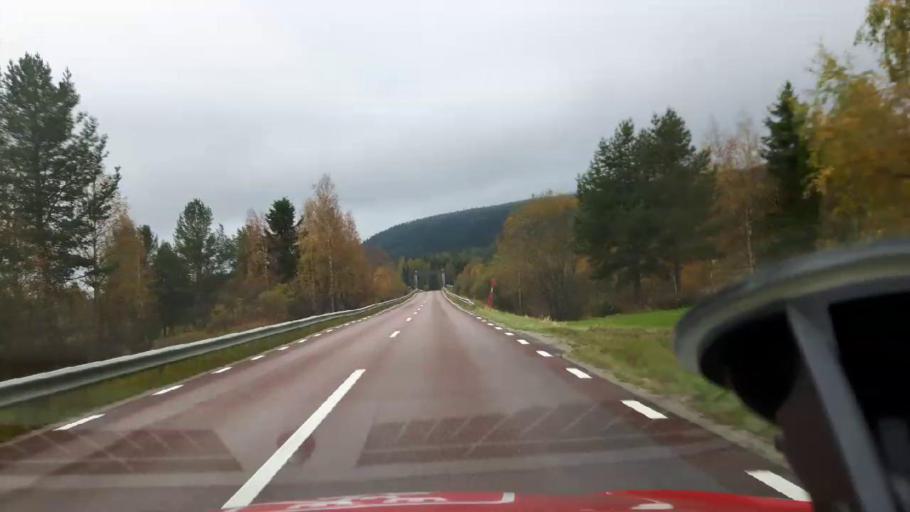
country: SE
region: Jaemtland
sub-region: Harjedalens Kommun
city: Sveg
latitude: 62.2763
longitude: 14.8060
